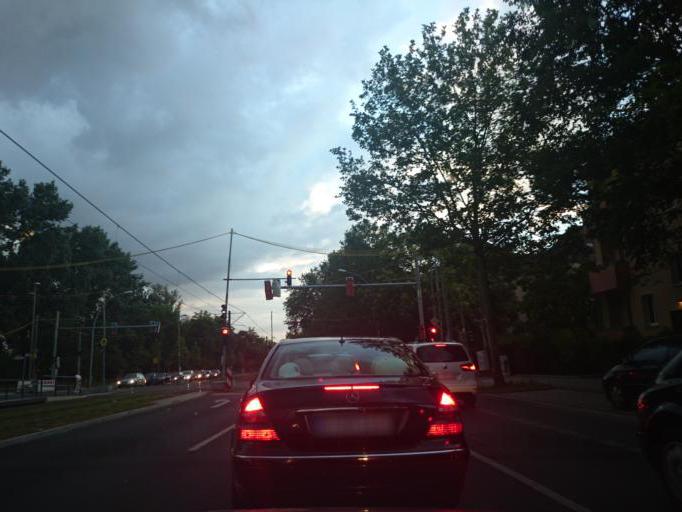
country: DE
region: Berlin
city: Friedrichsfelde
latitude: 52.5007
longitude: 13.5219
